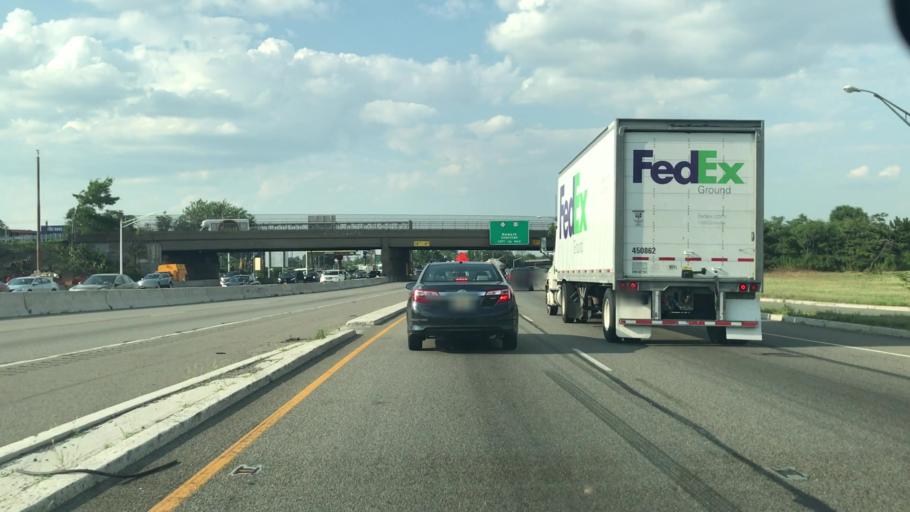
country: US
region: New Jersey
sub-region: Essex County
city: Newark
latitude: 40.7012
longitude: -74.1854
